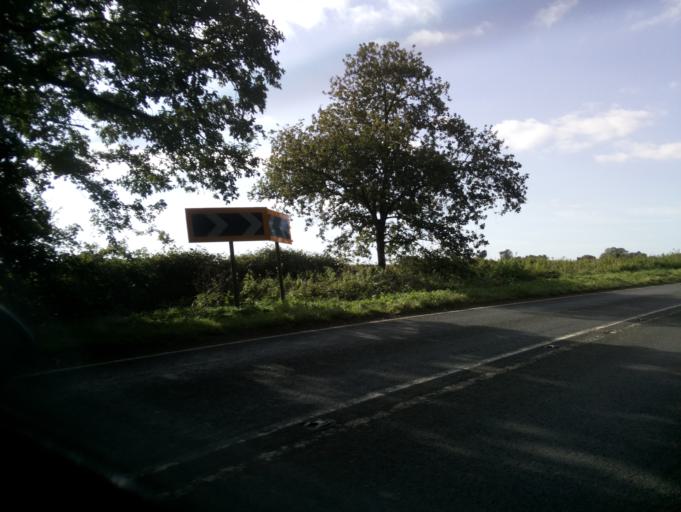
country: GB
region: England
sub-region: Hampshire
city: Basingstoke
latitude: 51.2335
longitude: -1.0760
